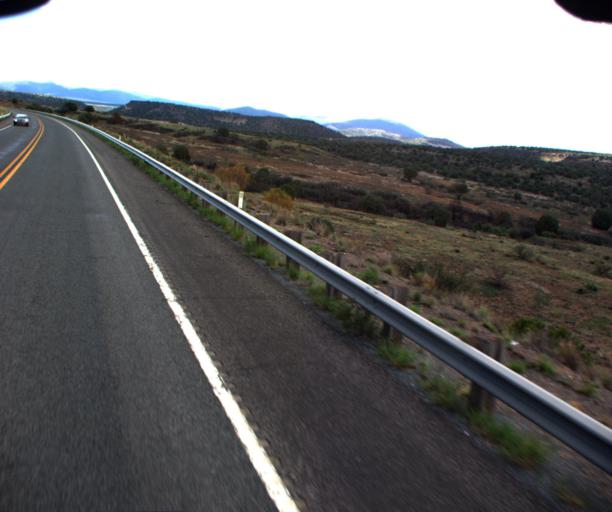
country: US
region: Arizona
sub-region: Yavapai County
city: Camp Verde
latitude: 34.5152
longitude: -112.0202
